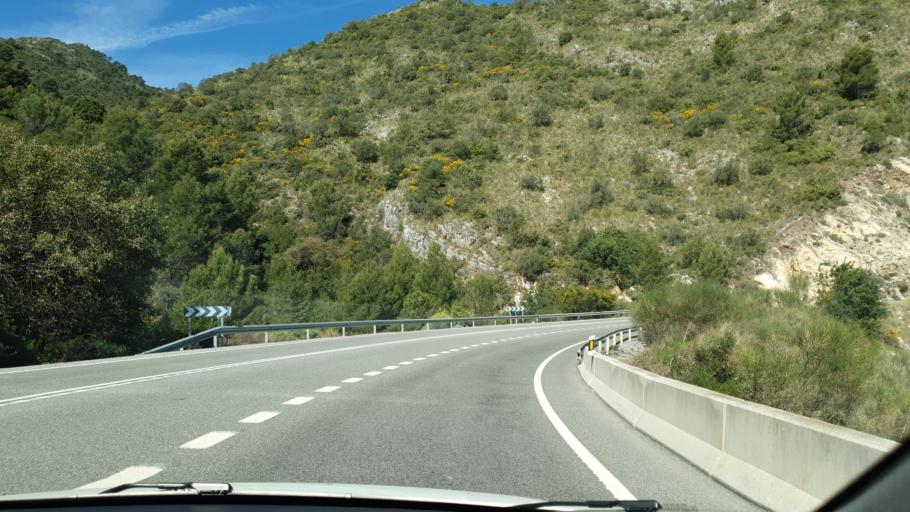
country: ES
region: Andalusia
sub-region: Provincia de Malaga
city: Ojen
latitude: 36.5556
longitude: -4.8648
